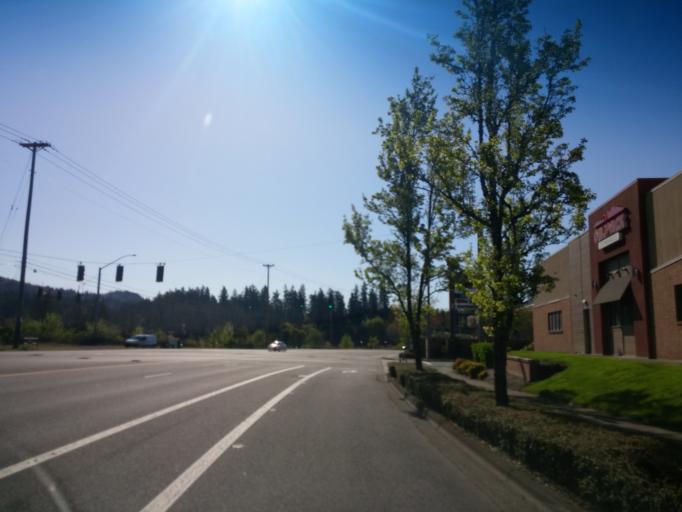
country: US
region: Oregon
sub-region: Washington County
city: Cedar Hills
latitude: 45.5158
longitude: -122.7907
